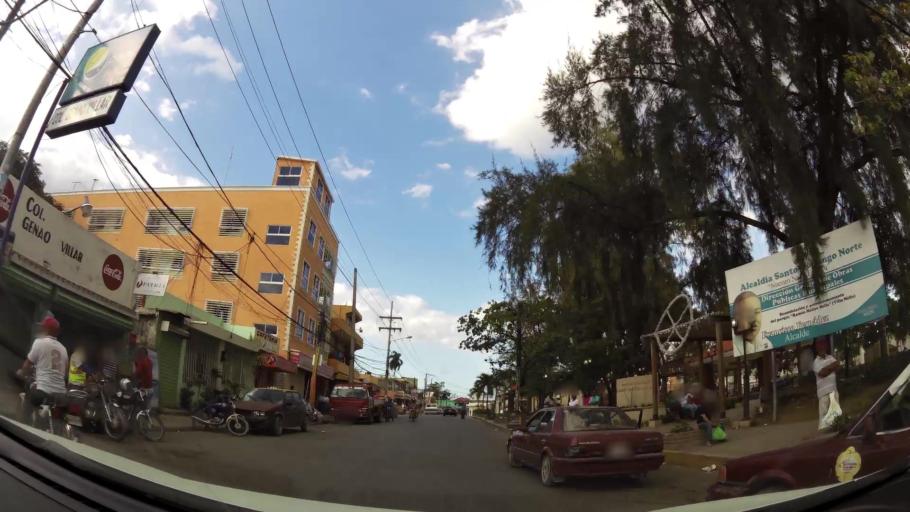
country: DO
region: Nacional
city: Ensanche Luperon
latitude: 18.5515
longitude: -69.9003
